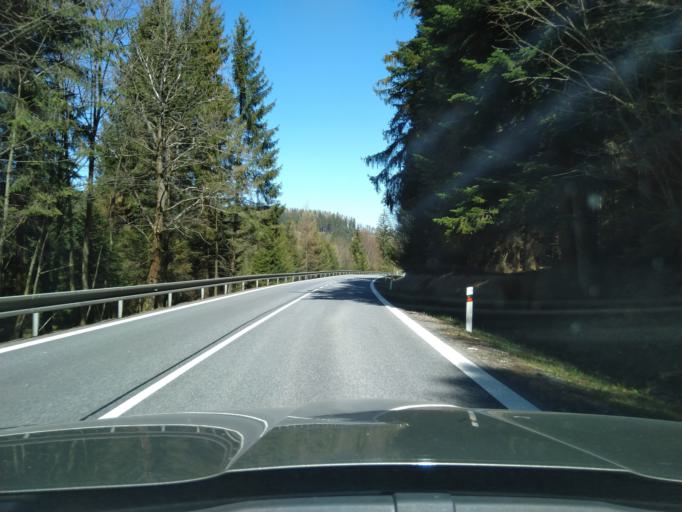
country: CZ
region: Jihocesky
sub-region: Okres Prachatice
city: Vimperk
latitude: 49.0419
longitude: 13.7607
